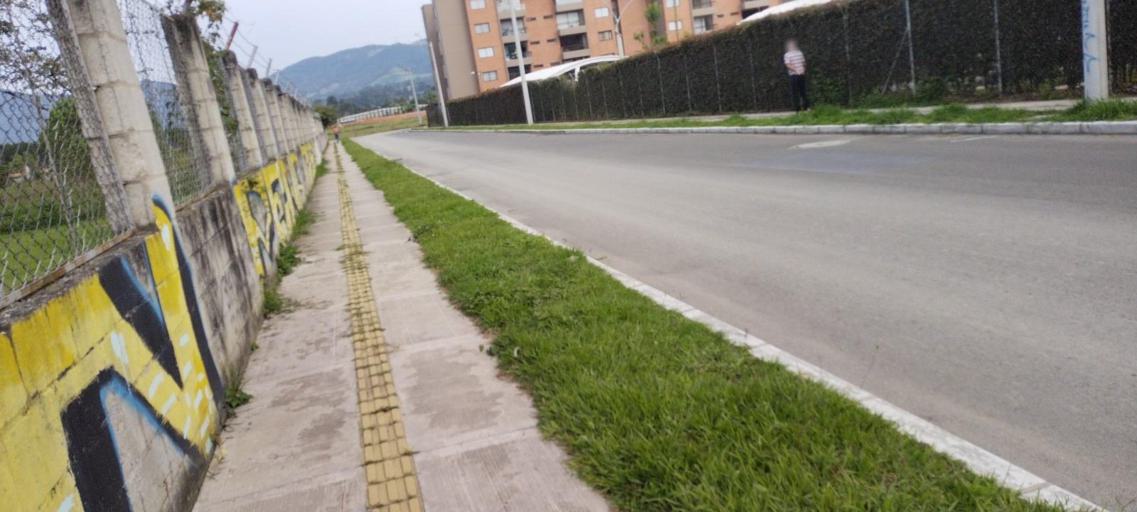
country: CO
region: Antioquia
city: La Ceja
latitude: 6.0295
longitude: -75.4230
